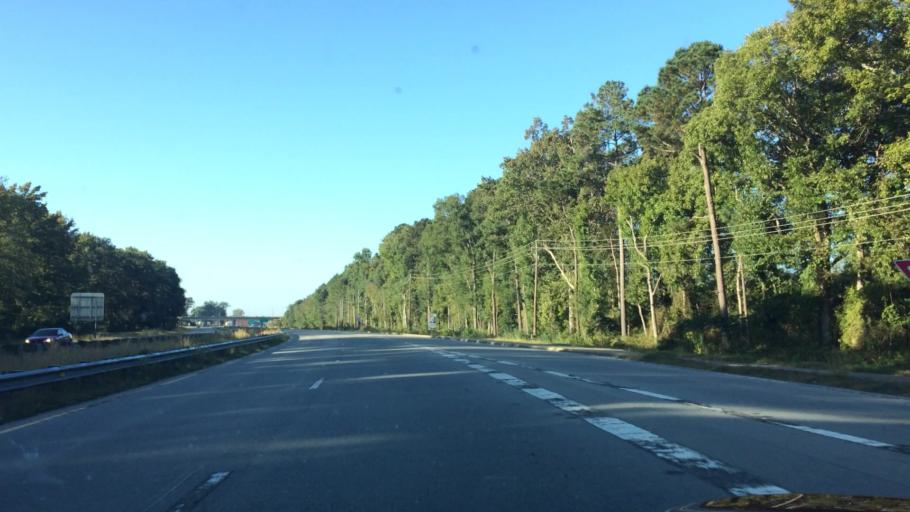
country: US
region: North Carolina
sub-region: Wayne County
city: Goldsboro
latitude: 35.3942
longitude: -78.0055
